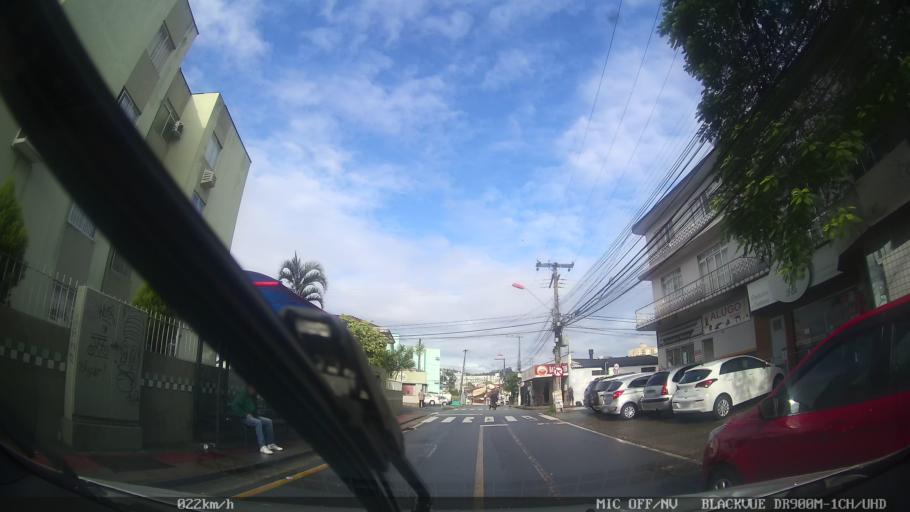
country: BR
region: Santa Catarina
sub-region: Sao Jose
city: Campinas
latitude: -27.6044
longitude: -48.6274
